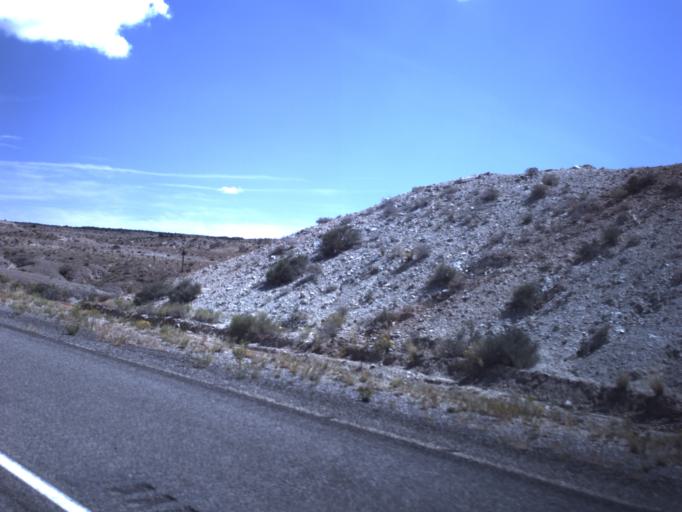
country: US
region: Utah
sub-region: Emery County
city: Ferron
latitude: 38.8444
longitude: -110.9866
